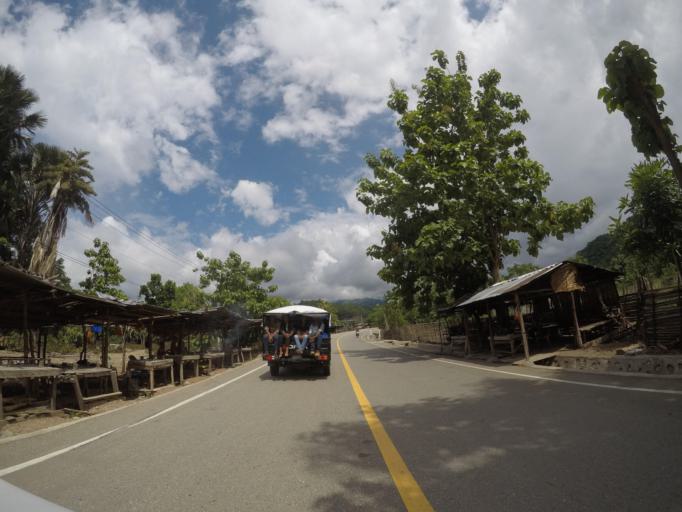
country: TL
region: Liquica
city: Maubara
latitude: -8.7959
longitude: 125.0994
